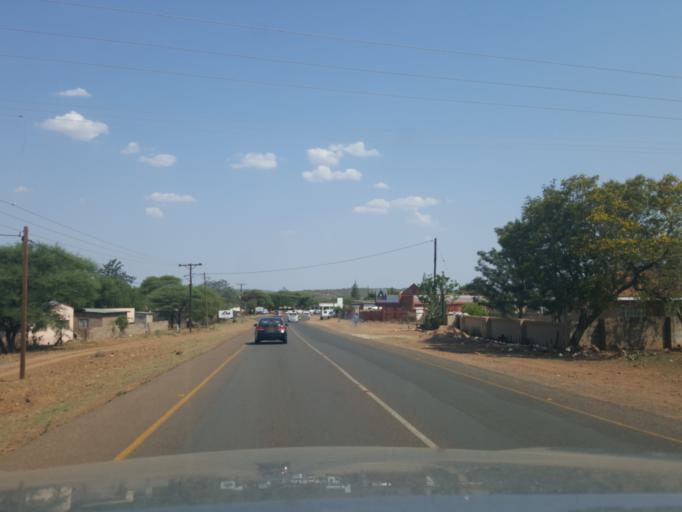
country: BW
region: South East
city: Ramotswa
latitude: -24.8467
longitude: 25.8292
